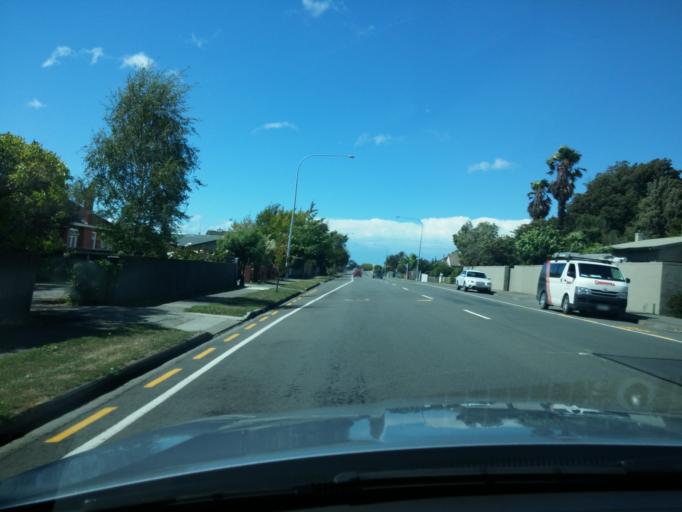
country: NZ
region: Marlborough
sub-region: Marlborough District
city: Blenheim
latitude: -41.5086
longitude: 173.9467
